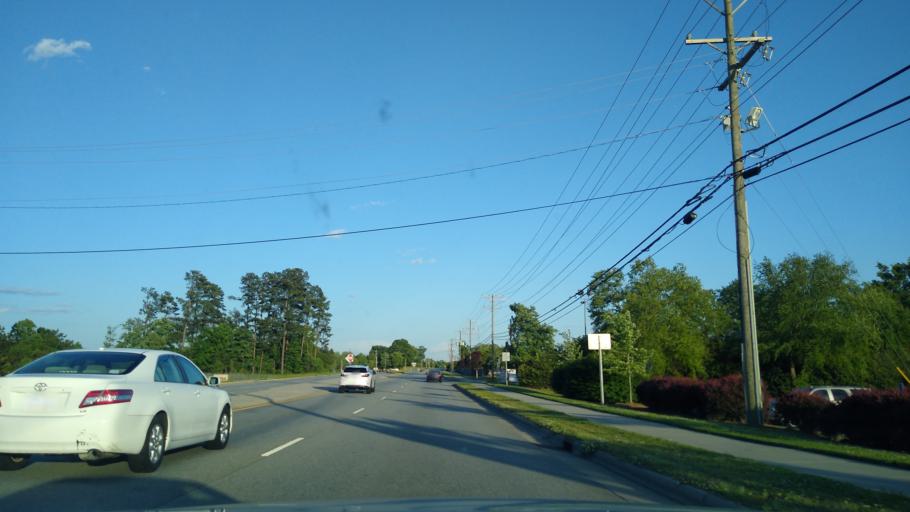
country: US
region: North Carolina
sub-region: Guilford County
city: Oak Ridge
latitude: 36.1032
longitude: -79.9830
